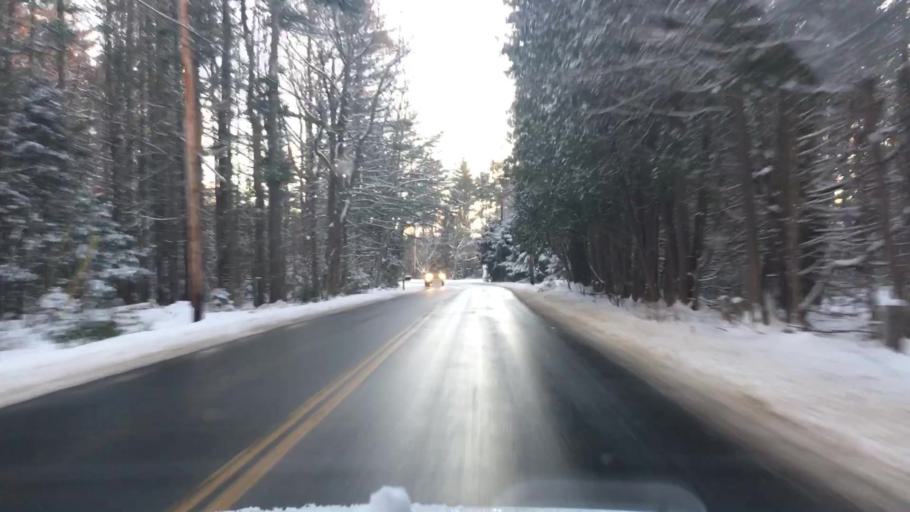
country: US
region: Maine
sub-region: Cumberland County
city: Brunswick
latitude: 43.9529
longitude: -69.9299
